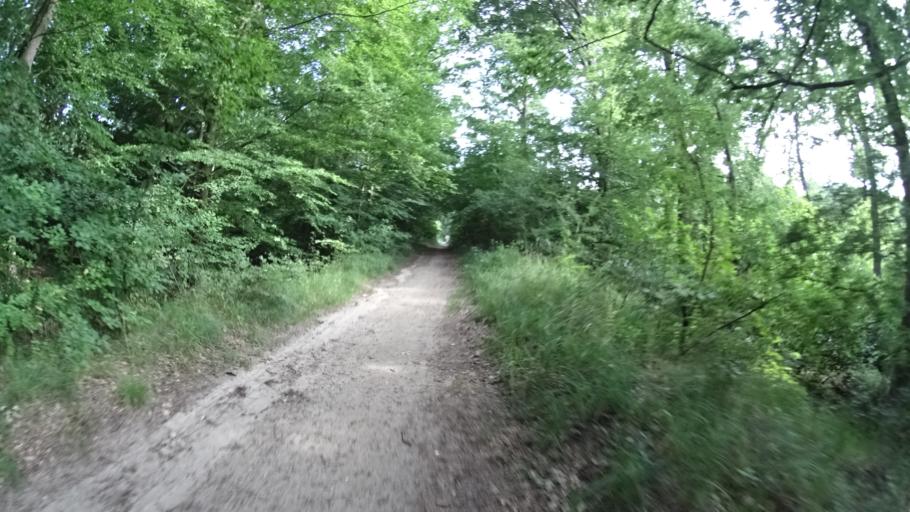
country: DE
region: Lower Saxony
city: Vogelsen
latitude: 53.2797
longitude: 10.3630
